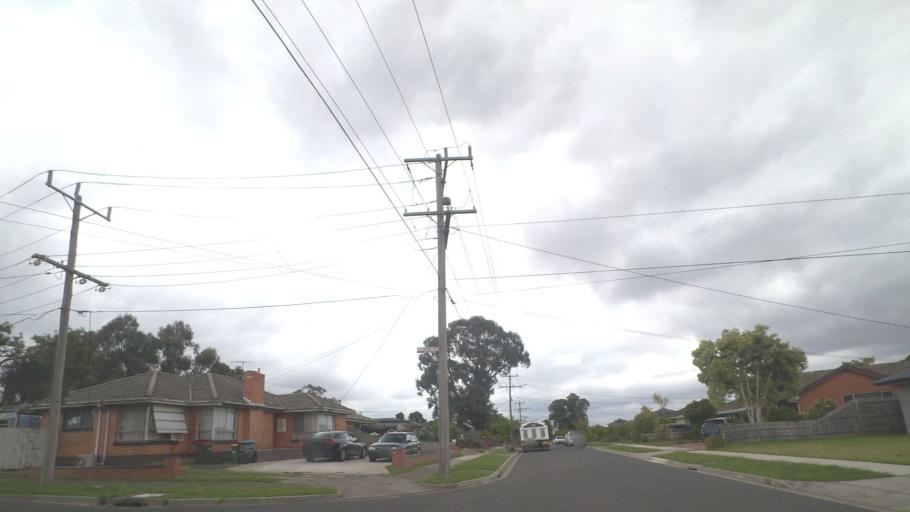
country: AU
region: Victoria
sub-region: Maroondah
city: Heathmont
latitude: -37.8469
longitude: 145.2518
